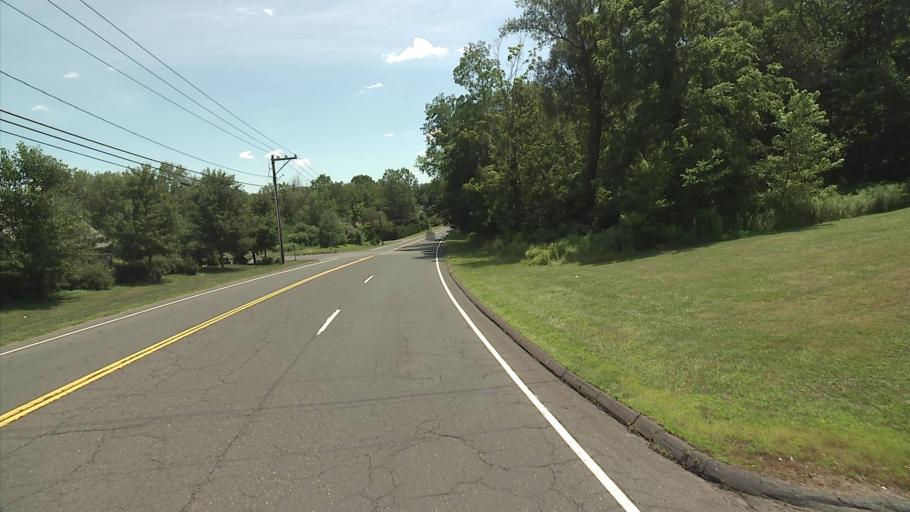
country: US
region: Connecticut
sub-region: Middlesex County
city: Cromwell
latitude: 41.6055
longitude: -72.6672
